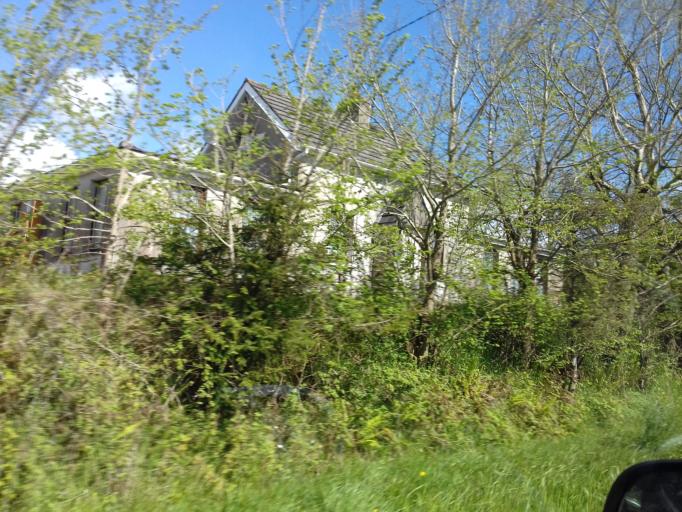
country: IE
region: Leinster
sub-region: Loch Garman
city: Castlebridge
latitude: 52.3849
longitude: -6.4197
